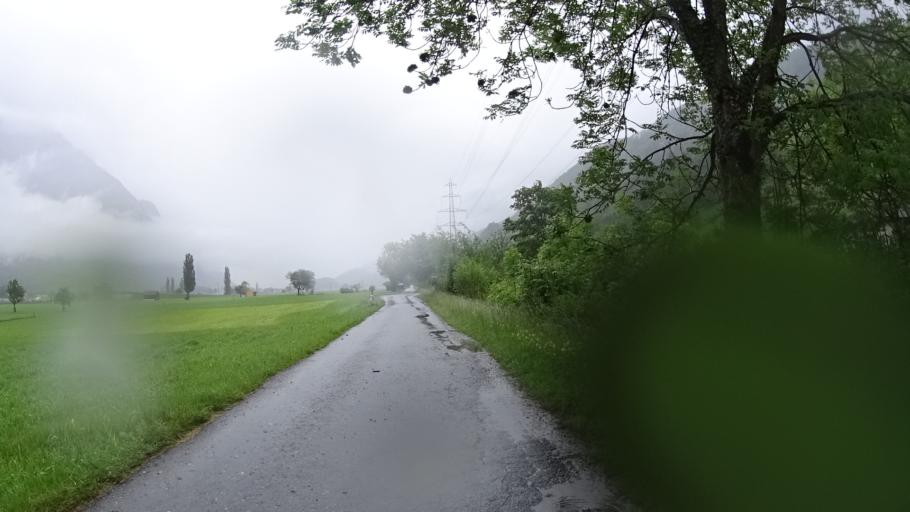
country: CH
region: Saint Gallen
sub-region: Wahlkreis Sarganserland
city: Flums
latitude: 47.0813
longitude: 9.3630
